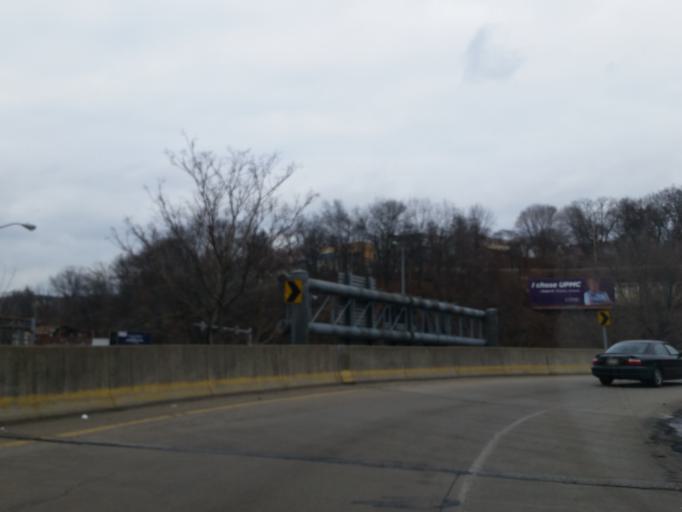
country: US
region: Pennsylvania
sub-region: Allegheny County
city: Mount Oliver
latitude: 40.4140
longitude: -80.0108
